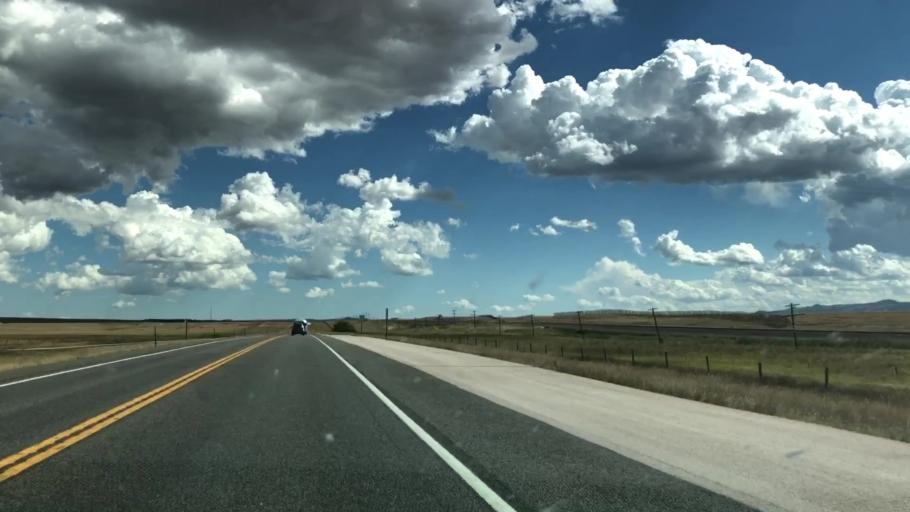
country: US
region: Wyoming
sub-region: Albany County
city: Laramie
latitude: 41.1617
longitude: -105.5786
